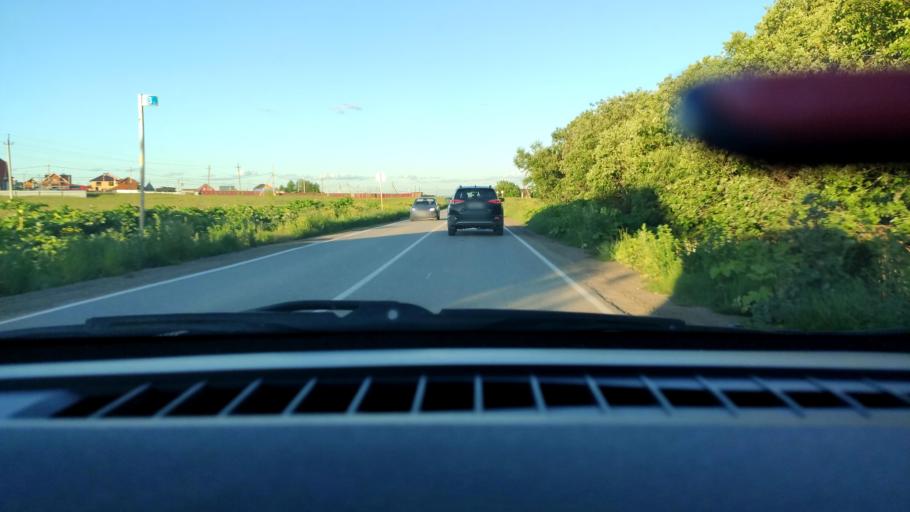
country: RU
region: Perm
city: Kultayevo
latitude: 57.9202
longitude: 55.9388
